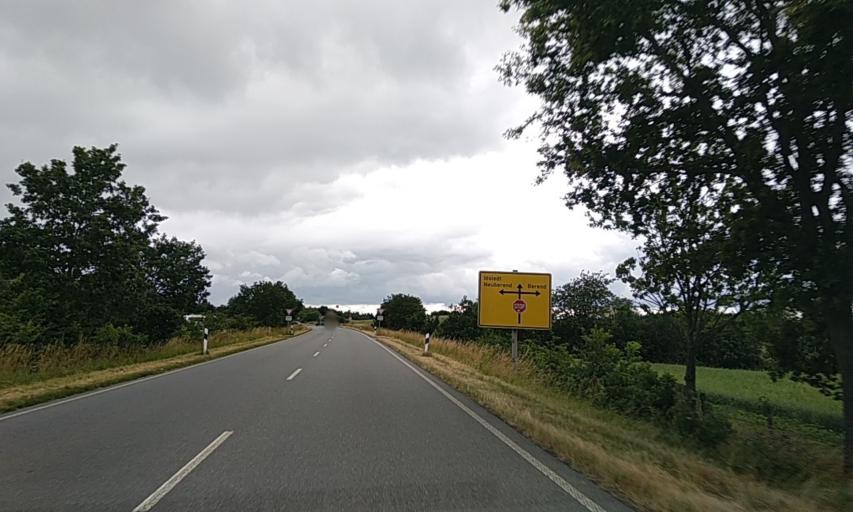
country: DE
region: Schleswig-Holstein
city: Neuberend
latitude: 54.5460
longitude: 9.5456
